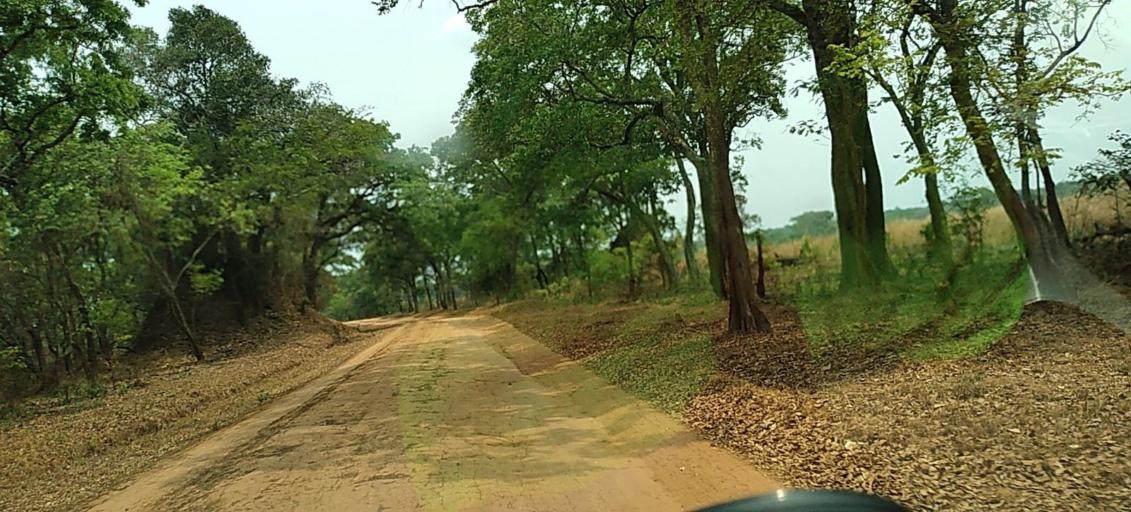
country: ZM
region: North-Western
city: Solwezi
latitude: -12.8154
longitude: 26.5362
